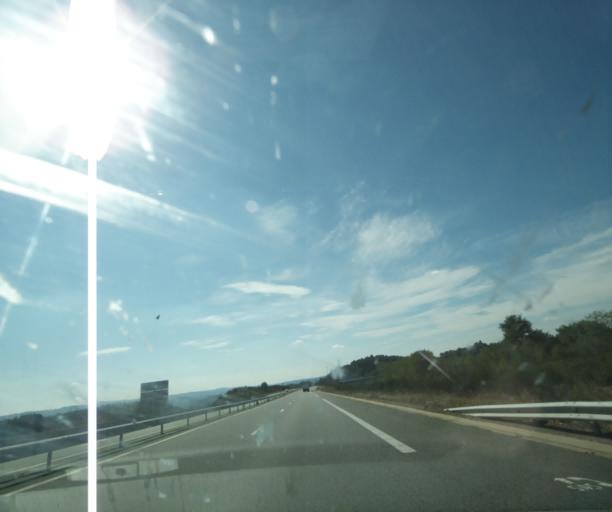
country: FR
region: Limousin
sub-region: Departement de la Correze
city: Naves
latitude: 45.3087
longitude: 1.8348
